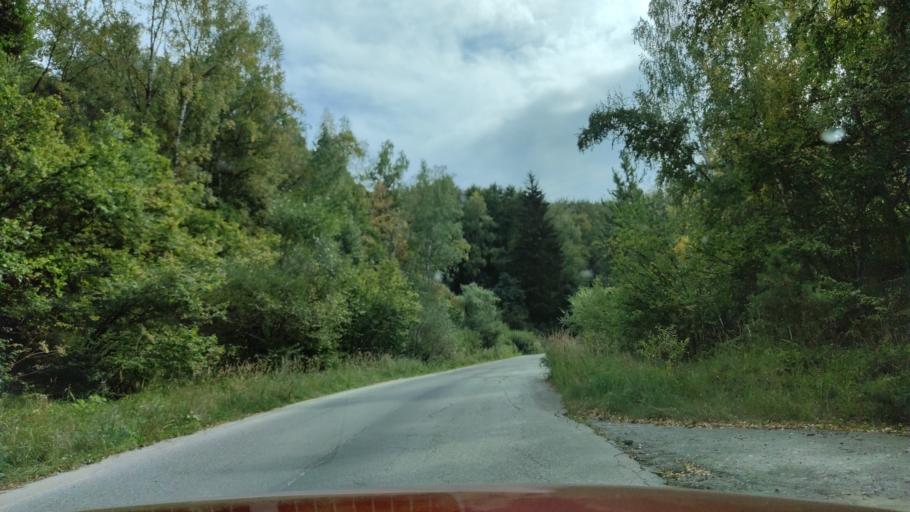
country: BG
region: Sofia-Capital
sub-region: Stolichna Obshtina
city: Sofia
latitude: 42.6199
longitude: 23.2261
